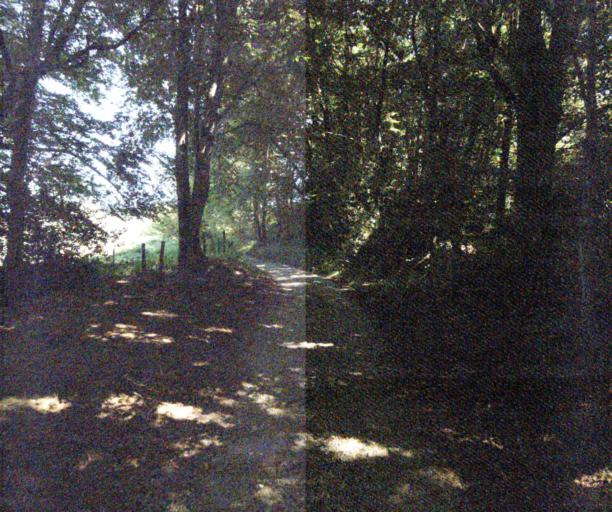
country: FR
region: Midi-Pyrenees
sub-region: Departement du Tarn
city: Soreze
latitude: 43.4425
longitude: 2.0964
